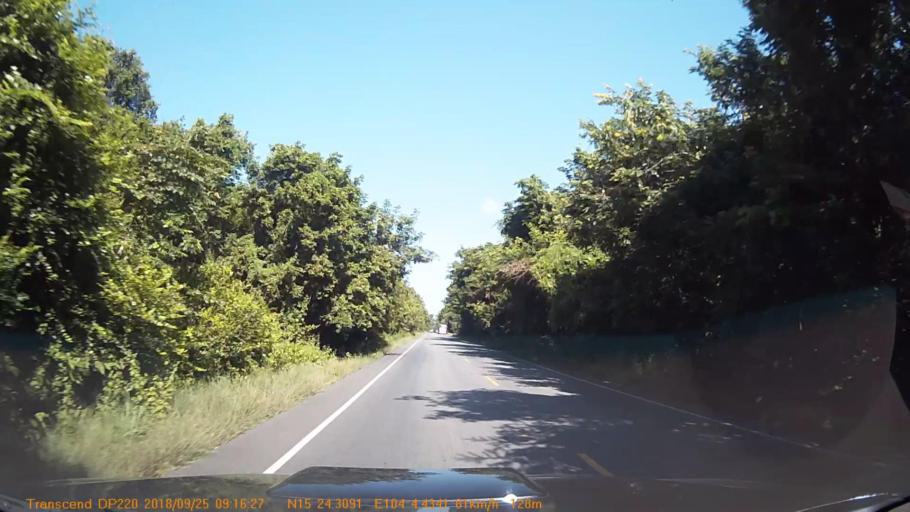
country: TH
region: Sisaket
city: Sila Lat
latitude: 15.4050
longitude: 104.0741
